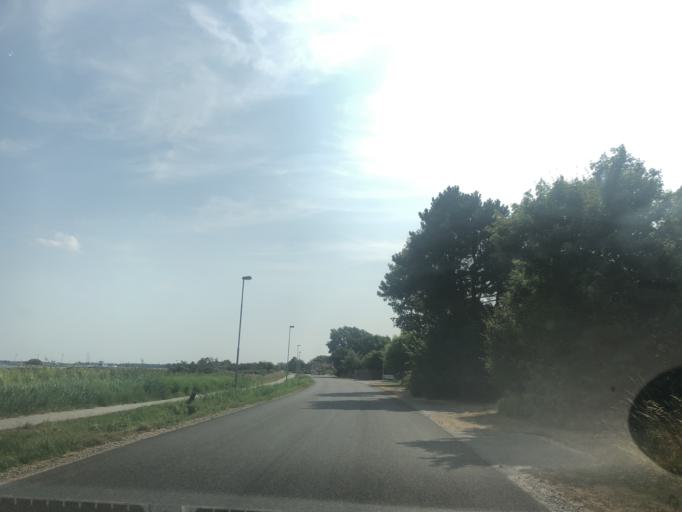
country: DK
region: North Denmark
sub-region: Morso Kommune
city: Nykobing Mors
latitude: 56.8120
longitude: 9.0223
